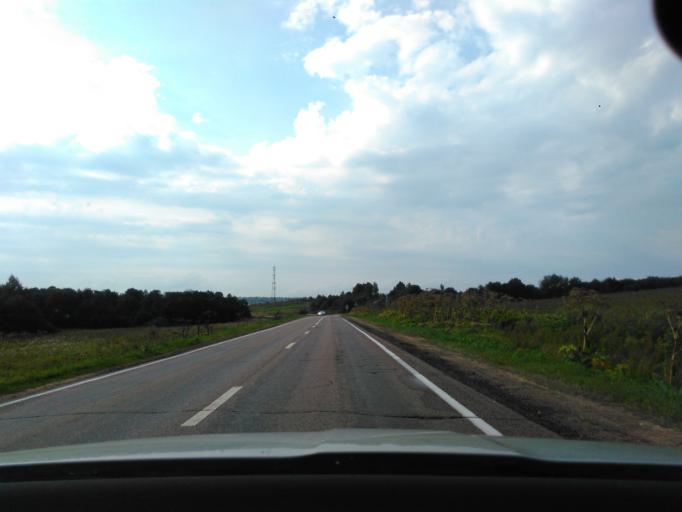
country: RU
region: Moskovskaya
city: Klin
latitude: 56.1551
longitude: 36.7646
